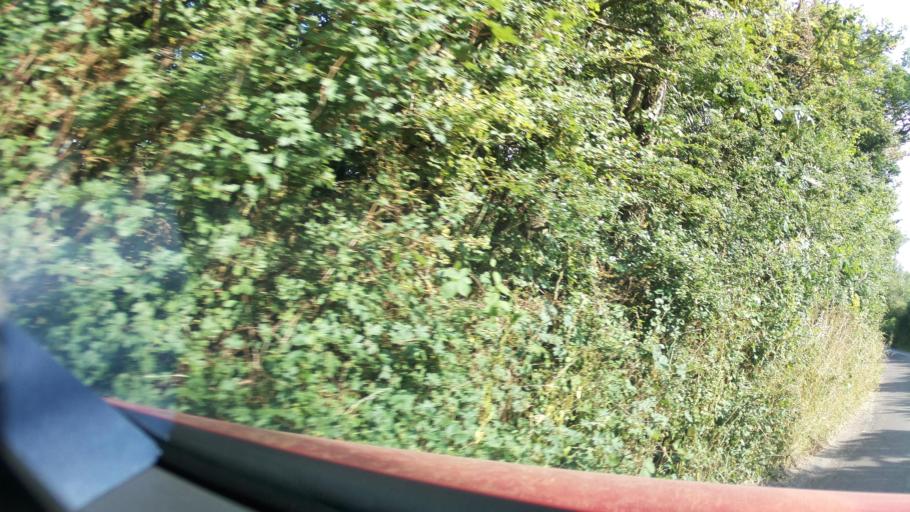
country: GB
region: England
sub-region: Wiltshire
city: Minety
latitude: 51.6236
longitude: -1.9697
